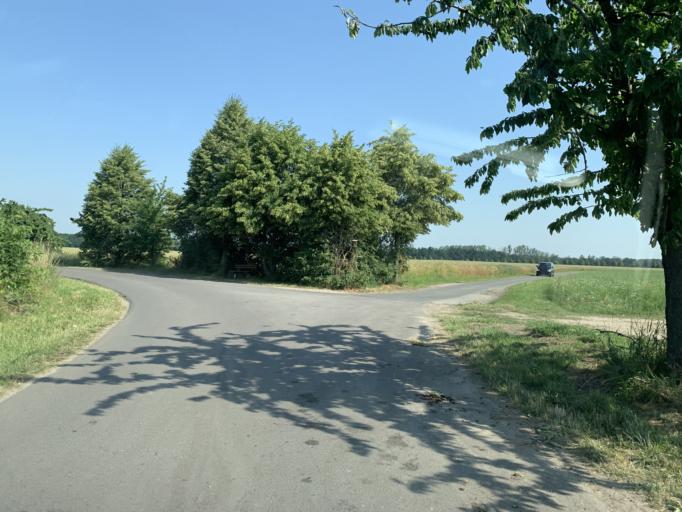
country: DE
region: Saxony-Anhalt
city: Erxleben
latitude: 52.2241
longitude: 11.2305
